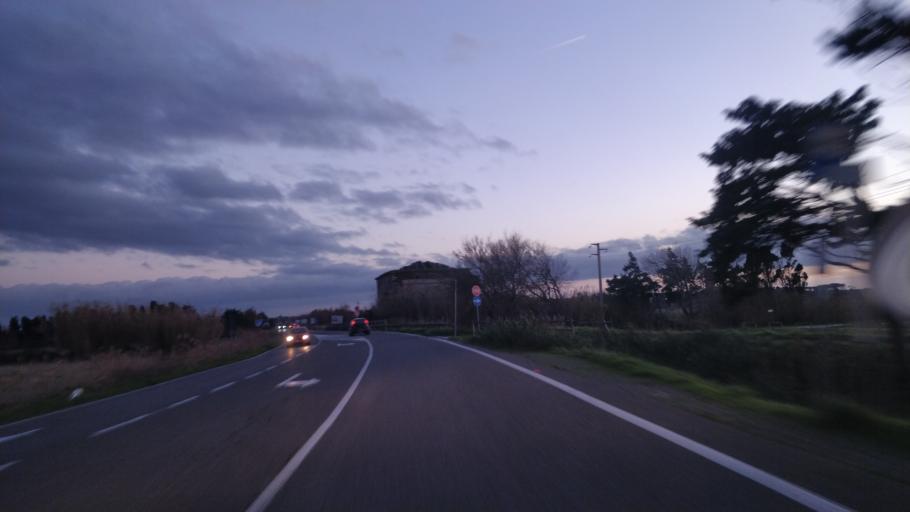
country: IT
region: Tuscany
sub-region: Provincia di Livorno
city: Vada
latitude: 43.3704
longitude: 10.4500
